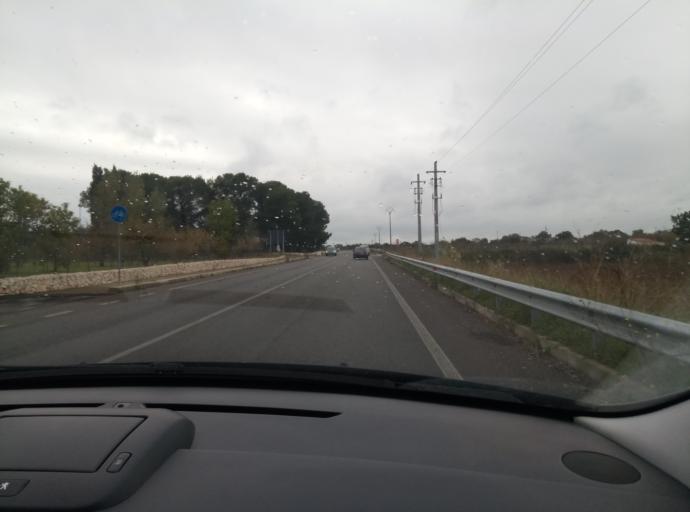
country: IT
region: Apulia
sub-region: Provincia di Bari
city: Acquaviva delle Fonti
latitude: 40.8808
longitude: 16.8112
